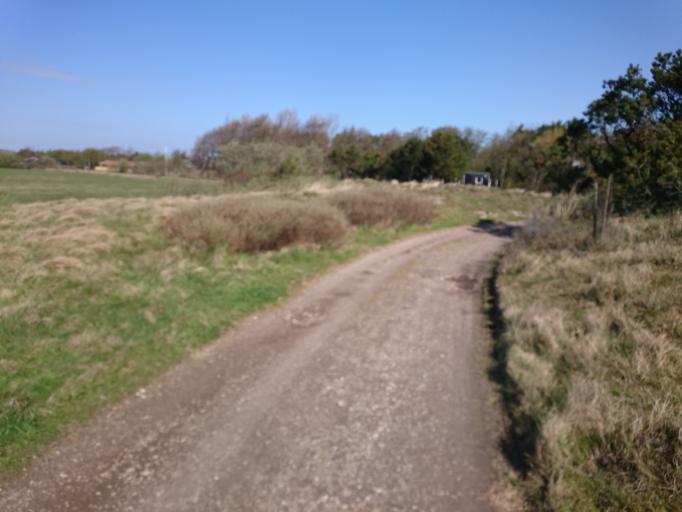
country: DK
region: South Denmark
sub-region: Fano Kommune
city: Nordby
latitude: 55.4410
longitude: 8.3823
